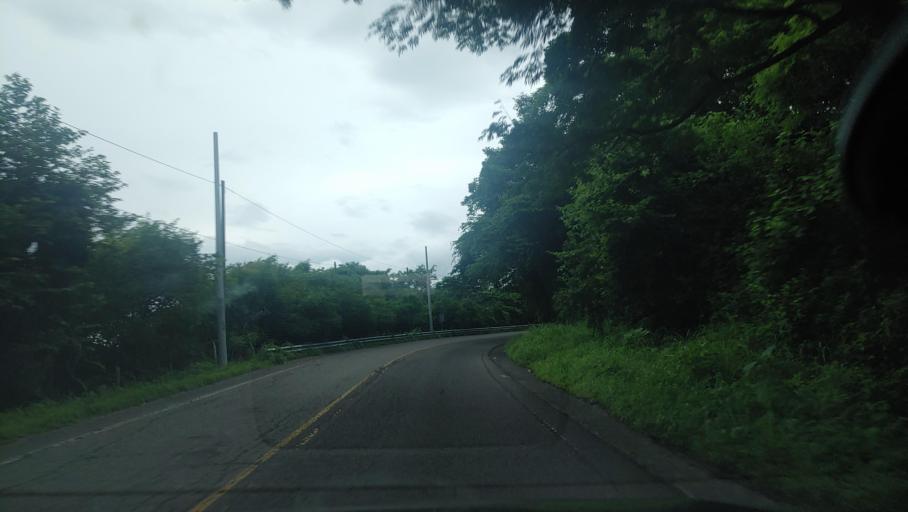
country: HN
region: Choluteca
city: Corpus
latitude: 13.3739
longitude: -87.0503
